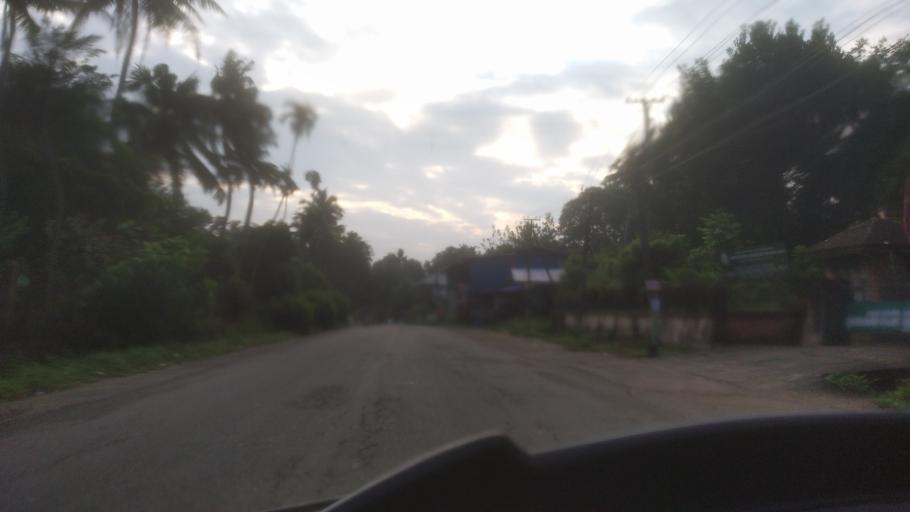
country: IN
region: Kerala
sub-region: Ernakulam
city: Kotamangalam
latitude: 10.0931
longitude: 76.5602
